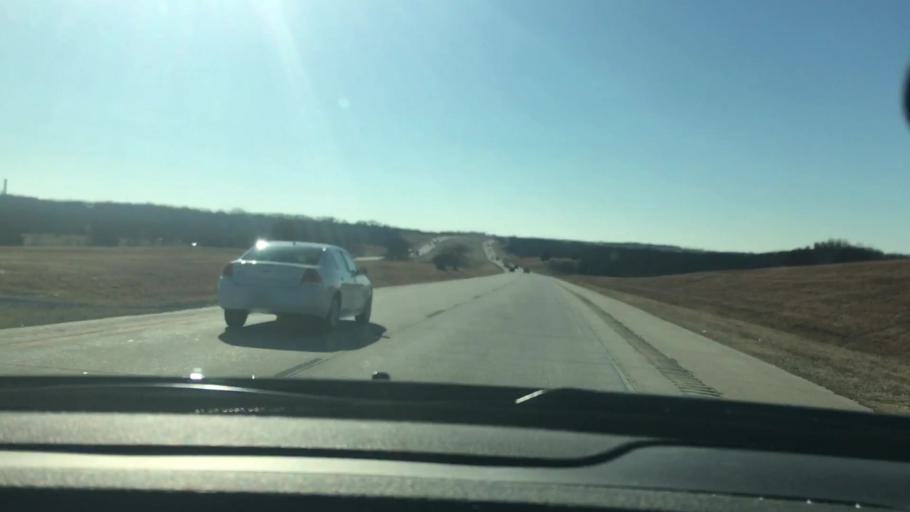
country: US
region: Oklahoma
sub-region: Love County
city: Marietta
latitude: 33.9944
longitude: -97.1407
